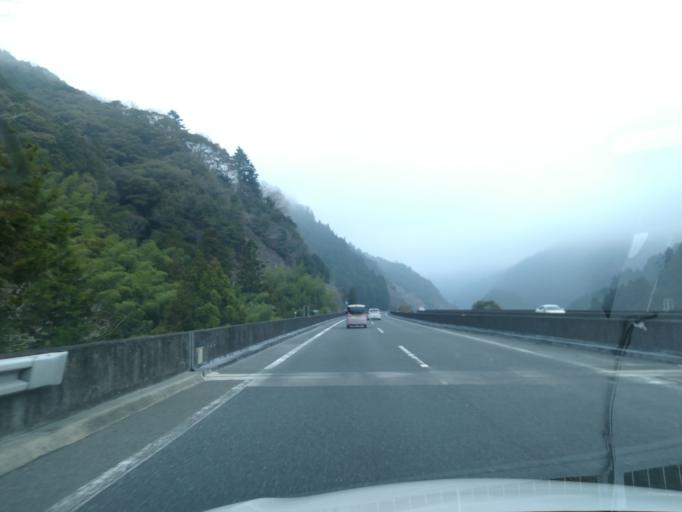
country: JP
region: Ehime
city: Kawanoecho
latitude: 33.7807
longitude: 133.6612
